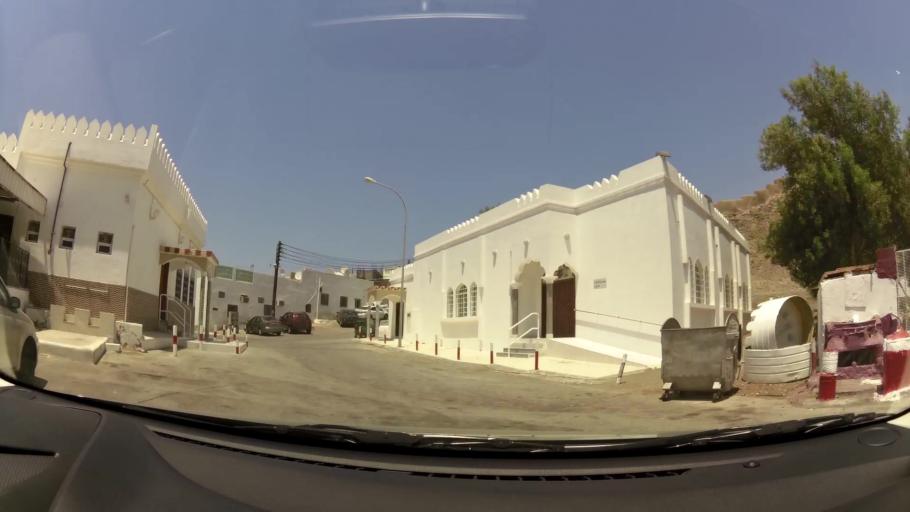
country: OM
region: Muhafazat Masqat
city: Muscat
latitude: 23.6210
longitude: 58.5596
